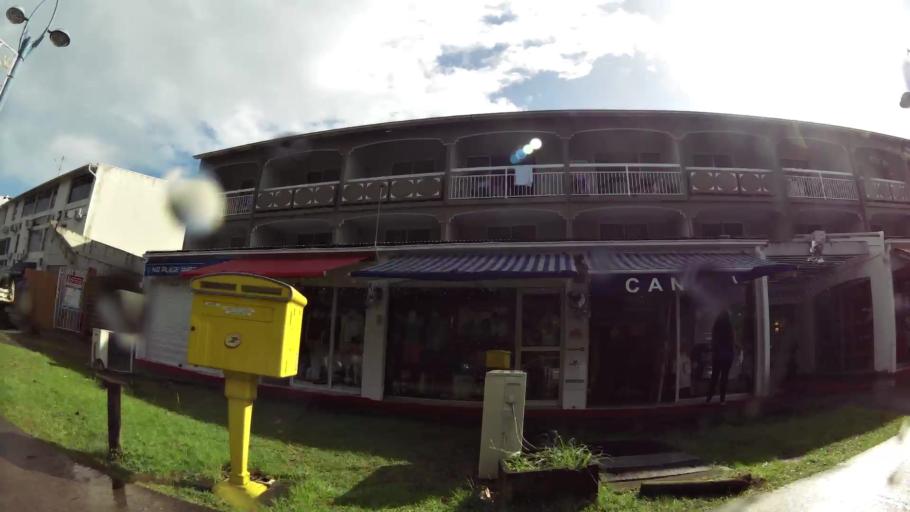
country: MQ
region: Martinique
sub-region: Martinique
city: Les Trois-Ilets
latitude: 14.5566
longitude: -61.0518
